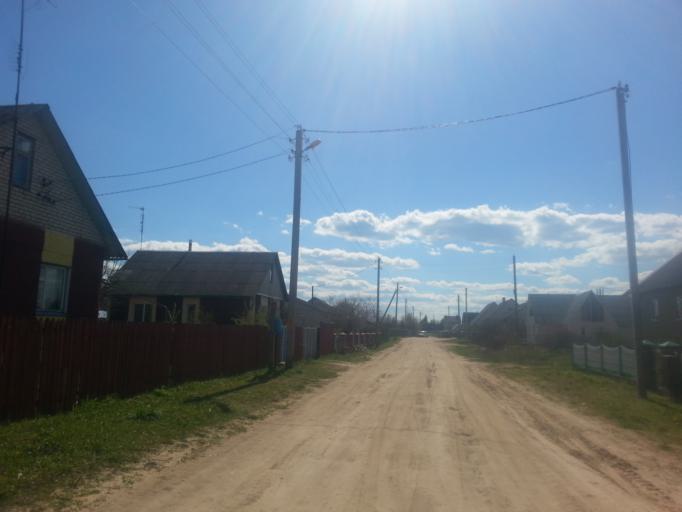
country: BY
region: Minsk
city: Narach
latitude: 54.9426
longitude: 26.6873
